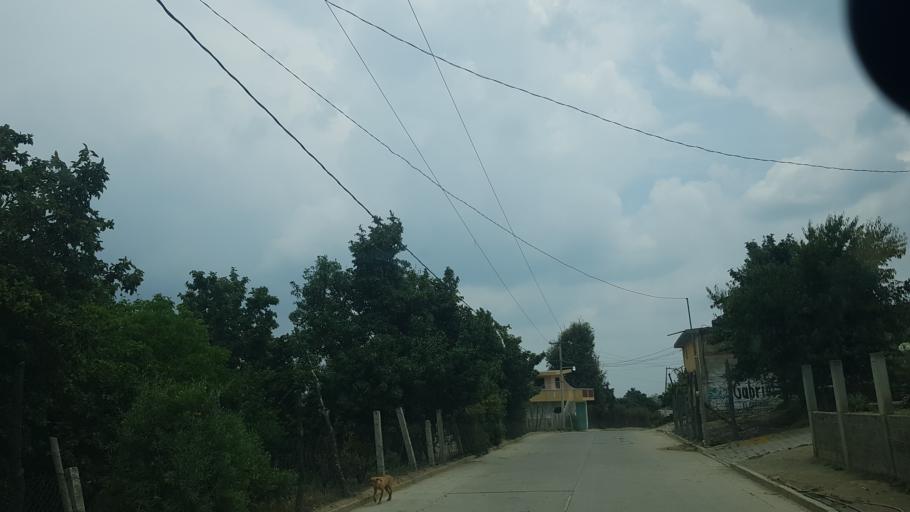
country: MX
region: Puebla
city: Domingo Arenas
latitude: 19.1530
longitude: -98.5051
